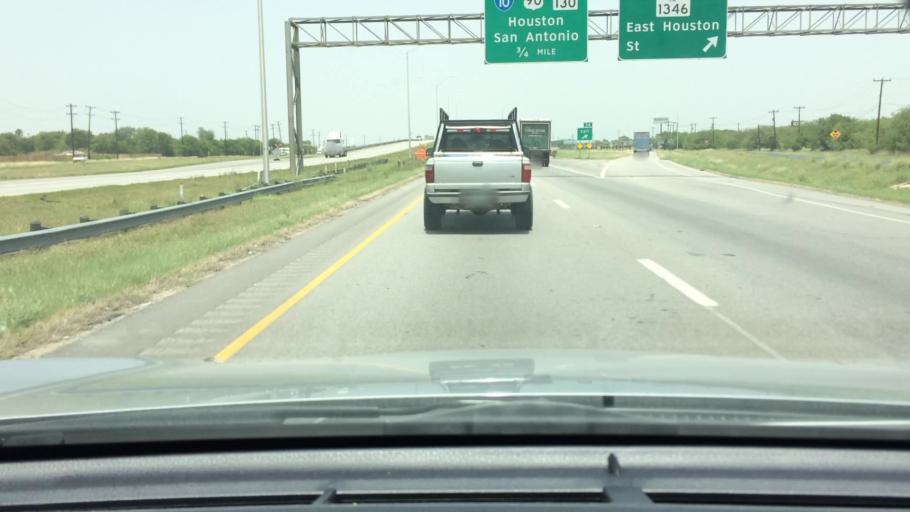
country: US
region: Texas
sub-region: Bexar County
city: Kirby
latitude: 29.4193
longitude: -98.3892
